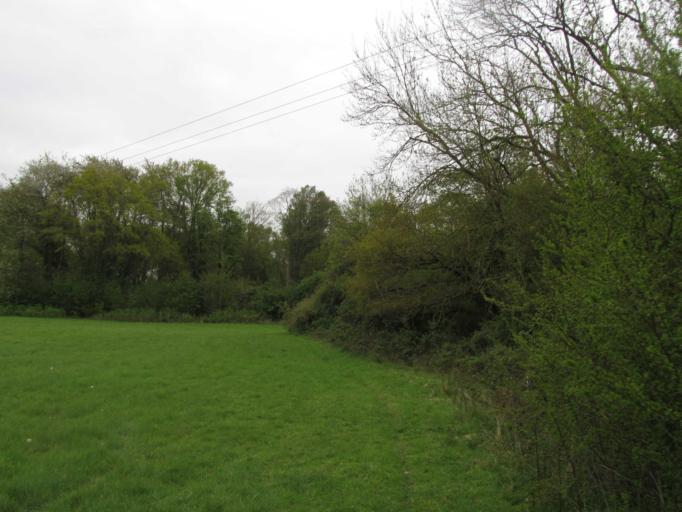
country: GB
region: England
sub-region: Royal Borough of Windsor and Maidenhead
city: Bisham
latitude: 51.5489
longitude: -0.7582
